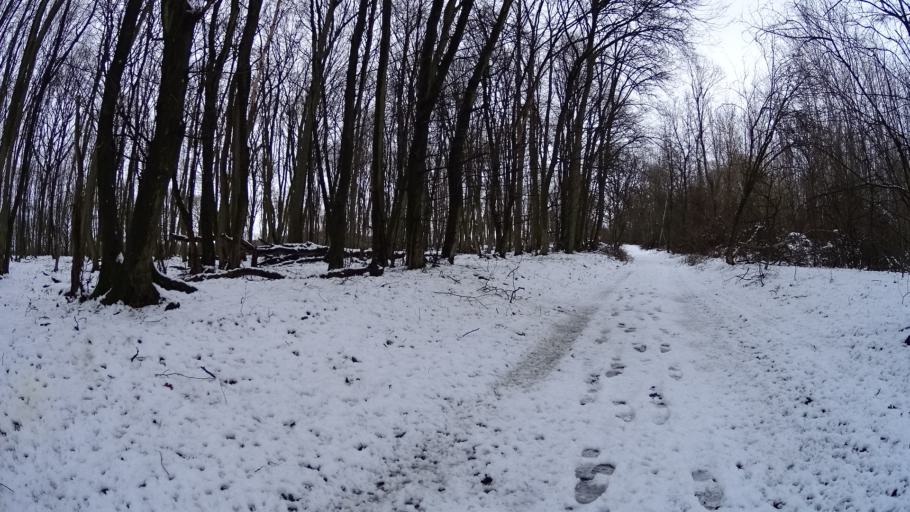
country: AT
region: Lower Austria
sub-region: Politischer Bezirk Korneuburg
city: Niederhollabrunn
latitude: 48.4170
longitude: 16.2986
